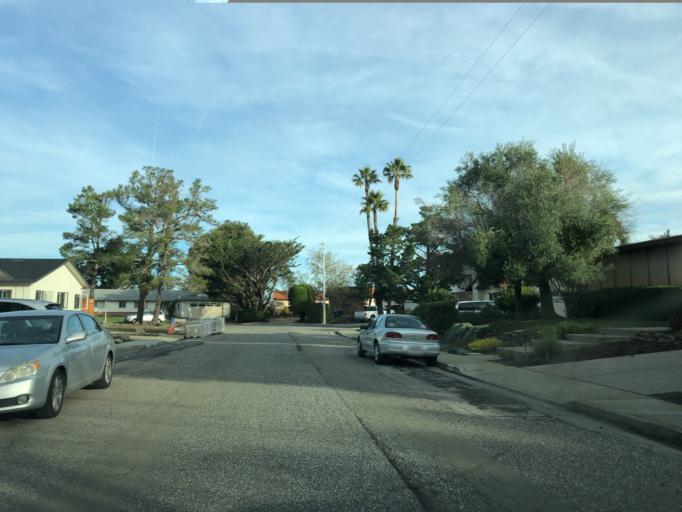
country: US
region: California
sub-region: San Mateo County
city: Highlands-Baywood Park
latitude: 37.5064
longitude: -122.3129
